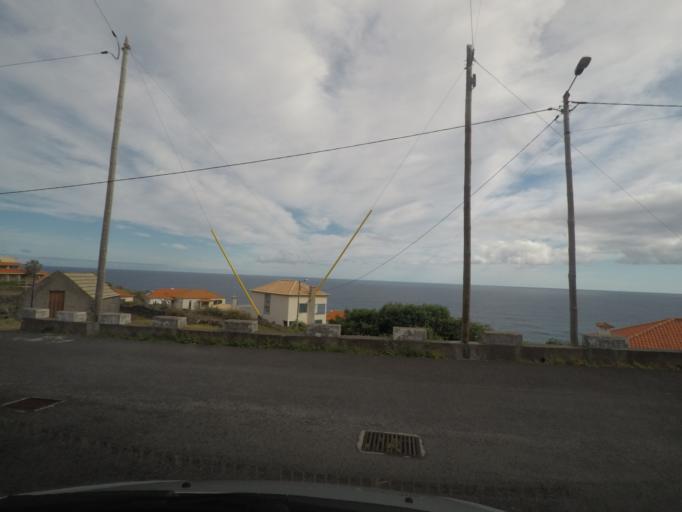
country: PT
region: Madeira
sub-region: Sao Vicente
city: Sao Vicente
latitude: 32.8283
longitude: -16.9892
